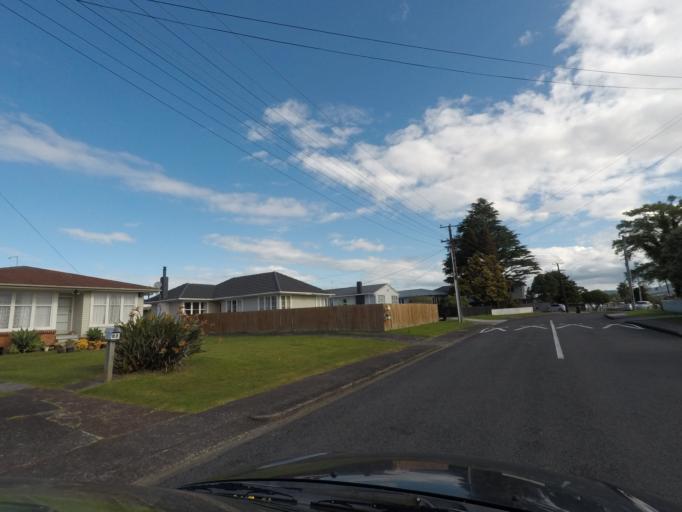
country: NZ
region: Auckland
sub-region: Auckland
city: Rosebank
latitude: -36.8702
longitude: 174.6424
